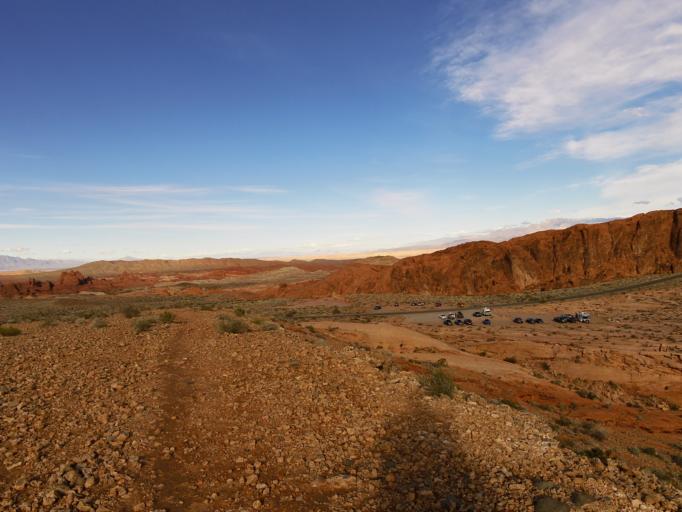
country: US
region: Nevada
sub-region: Clark County
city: Moapa Valley
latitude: 36.4873
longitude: -114.5308
